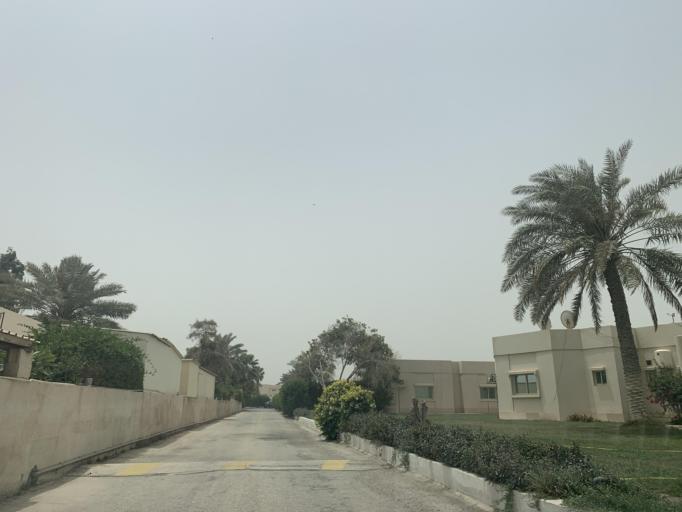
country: BH
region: Manama
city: Jidd Hafs
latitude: 26.2293
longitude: 50.5191
